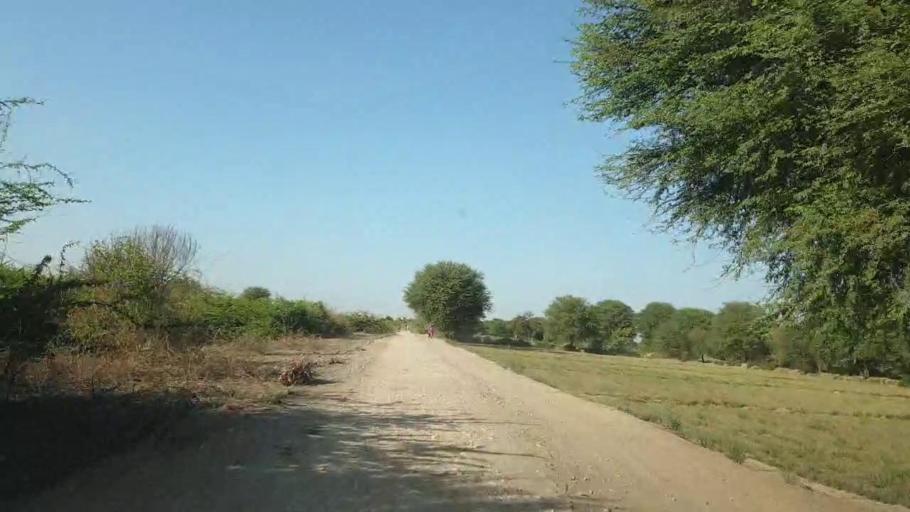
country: PK
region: Sindh
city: Kunri
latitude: 25.0520
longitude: 69.4420
